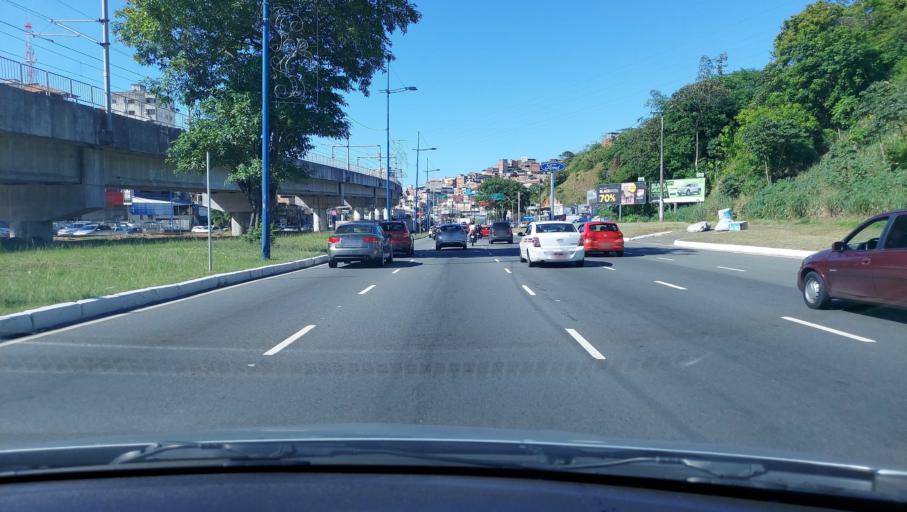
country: BR
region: Bahia
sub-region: Salvador
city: Salvador
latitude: -12.9780
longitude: -38.4800
